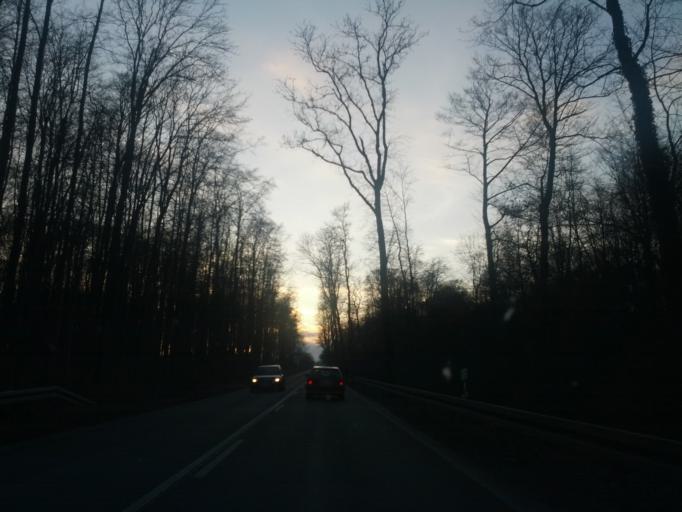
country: DE
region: Thuringia
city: Heyerode
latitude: 51.2100
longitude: 10.3483
